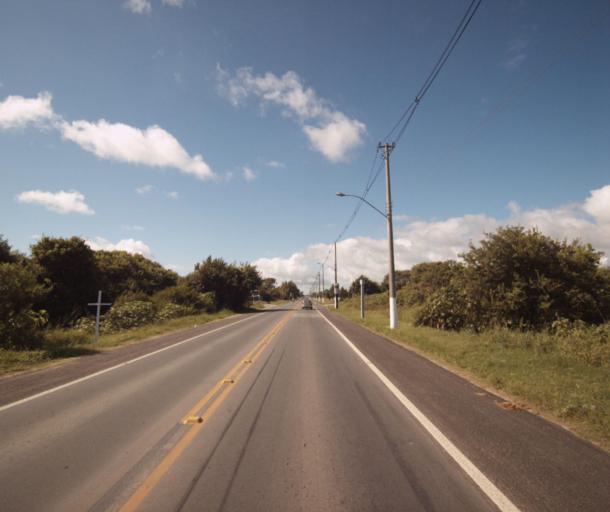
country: BR
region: Rio Grande do Sul
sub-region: Pelotas
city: Pelotas
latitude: -31.7521
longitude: -52.3593
